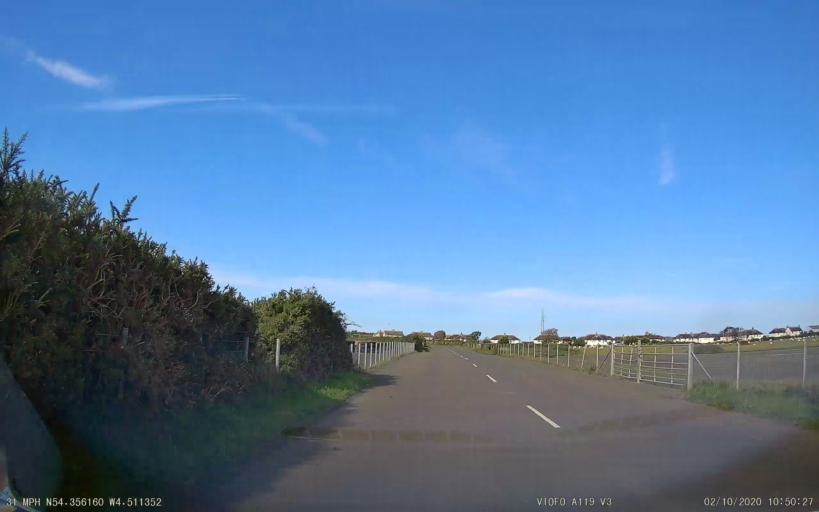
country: IM
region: Ramsey
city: Ramsey
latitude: 54.3563
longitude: -4.5108
